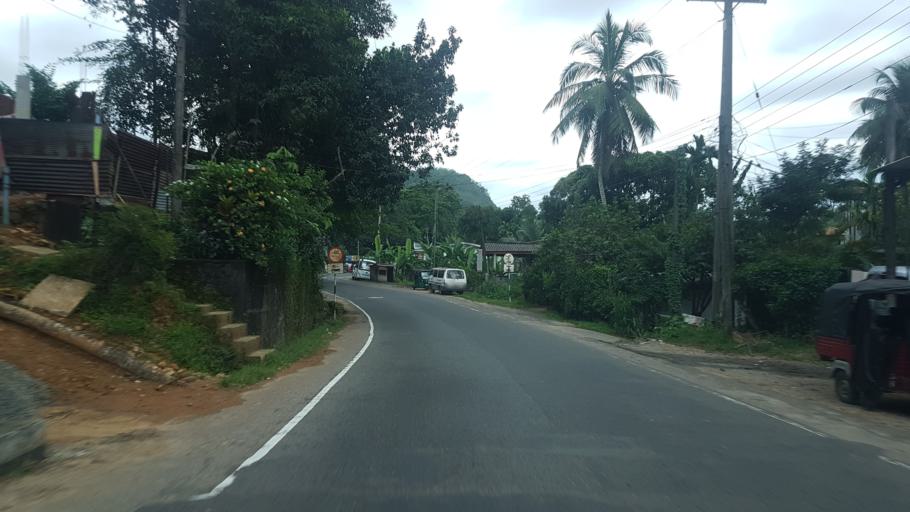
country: LK
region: Western
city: Hanwella Ihala
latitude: 7.0349
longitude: 80.2929
